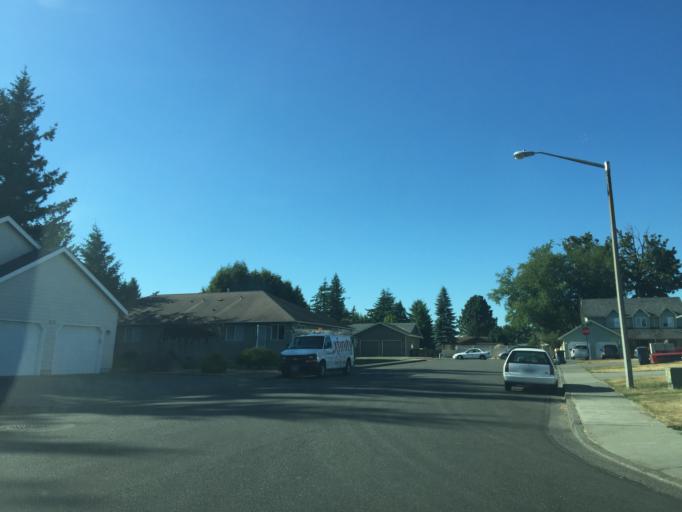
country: US
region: Washington
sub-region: Whatcom County
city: Lynden
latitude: 48.9504
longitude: -122.4344
